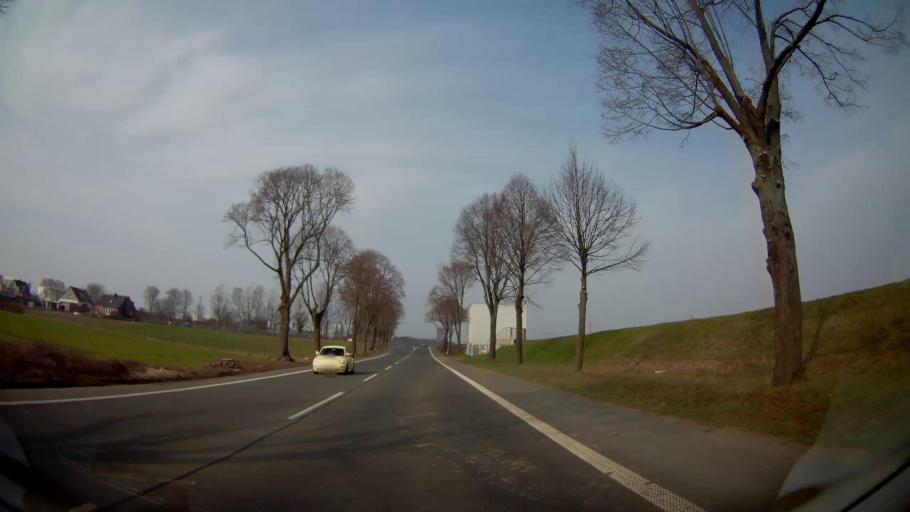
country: DE
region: North Rhine-Westphalia
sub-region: Regierungsbezirk Dusseldorf
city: Moers
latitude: 51.4697
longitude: 6.6884
